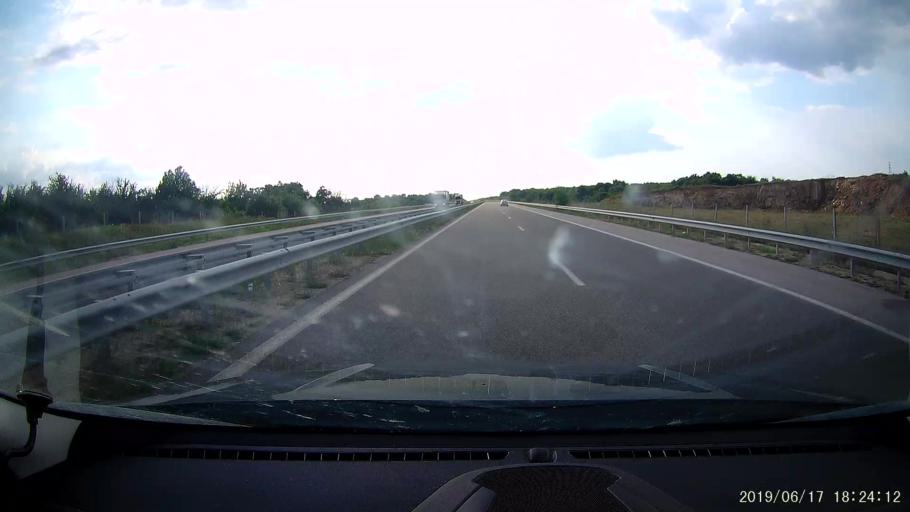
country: BG
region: Khaskovo
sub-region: Obshtina Dimitrovgrad
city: Dimitrovgrad
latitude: 41.9819
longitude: 25.6985
